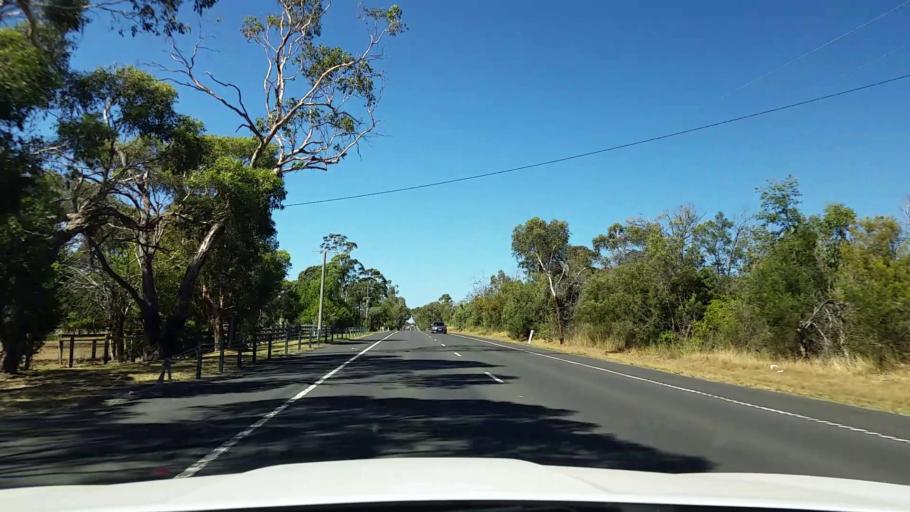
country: AU
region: Victoria
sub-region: Mornington Peninsula
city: Somerville
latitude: -38.2118
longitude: 145.1672
